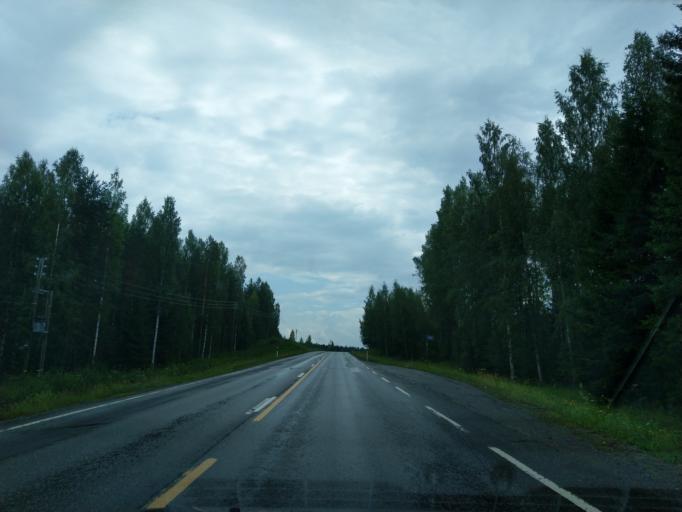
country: FI
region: Southern Savonia
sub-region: Savonlinna
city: Punkaharju
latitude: 61.6633
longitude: 29.4148
